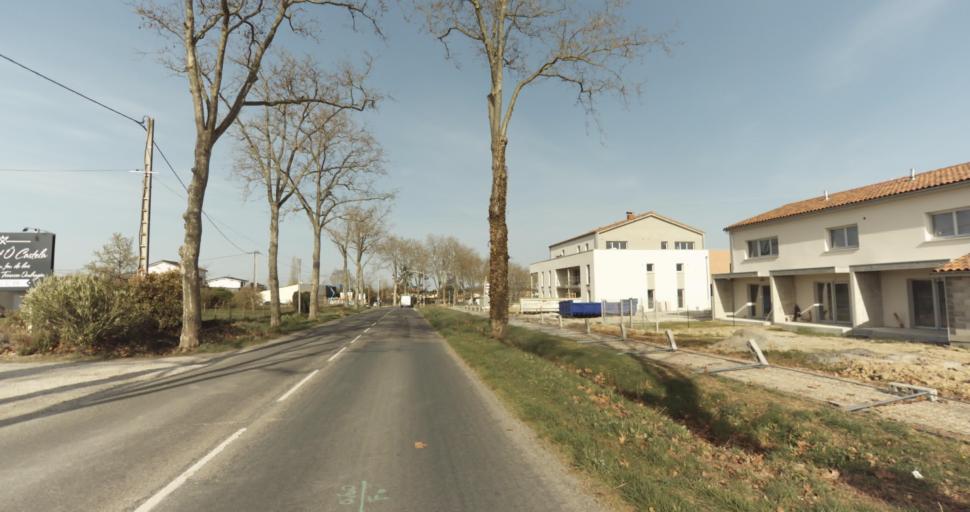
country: FR
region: Midi-Pyrenees
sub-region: Departement du Tarn
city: Saint-Sulpice-la-Pointe
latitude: 43.7612
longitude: 1.6998
